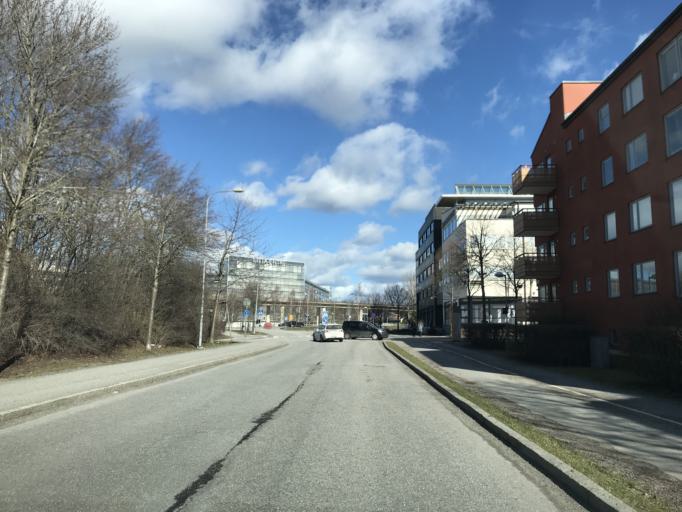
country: SE
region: Stockholm
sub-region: Stockholms Kommun
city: Kista
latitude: 59.3981
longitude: 17.9467
